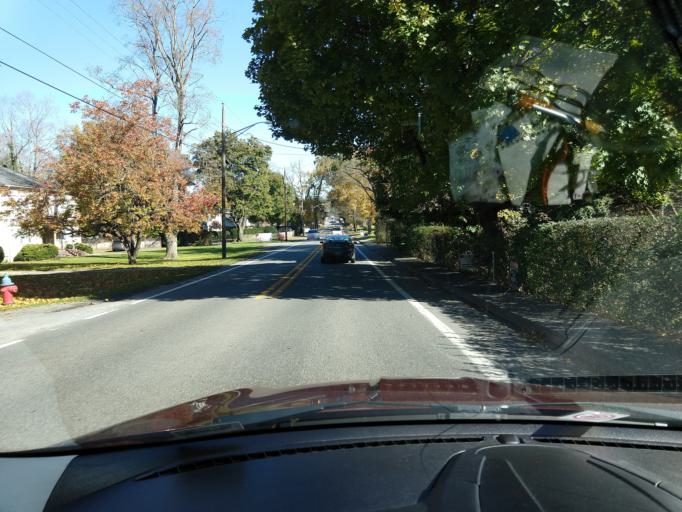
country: US
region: West Virginia
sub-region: Greenbrier County
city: Lewisburg
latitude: 37.7991
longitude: -80.4480
